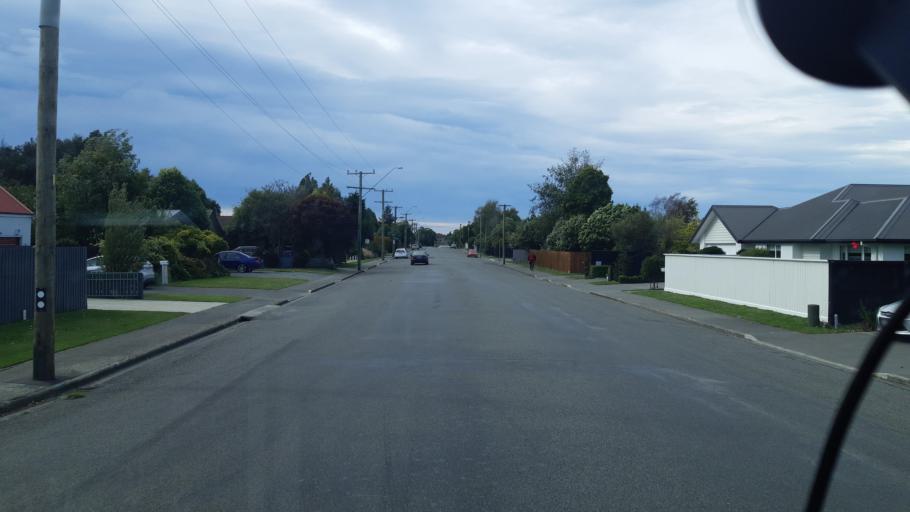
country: NZ
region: Canterbury
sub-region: Waimakariri District
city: Woodend
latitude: -43.3204
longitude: 172.6615
